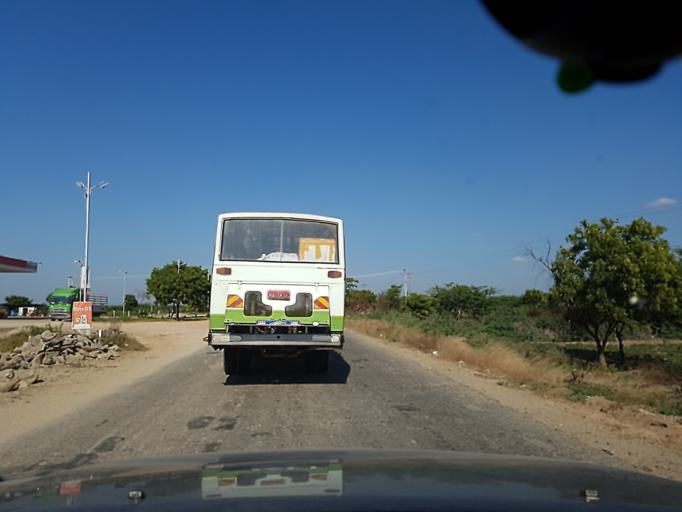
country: MM
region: Sagain
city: Monywa
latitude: 21.8773
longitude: 95.2709
